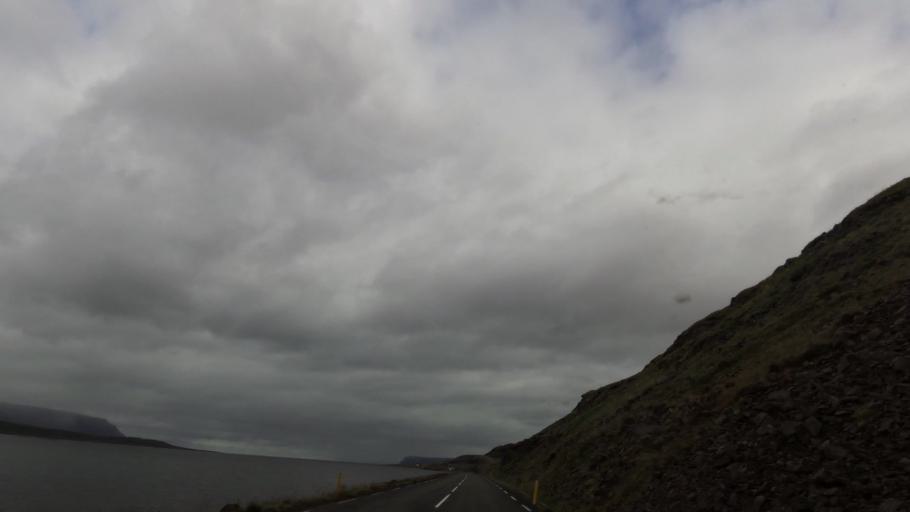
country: IS
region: Westfjords
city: Isafjoerdur
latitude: 65.9875
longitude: -22.7759
